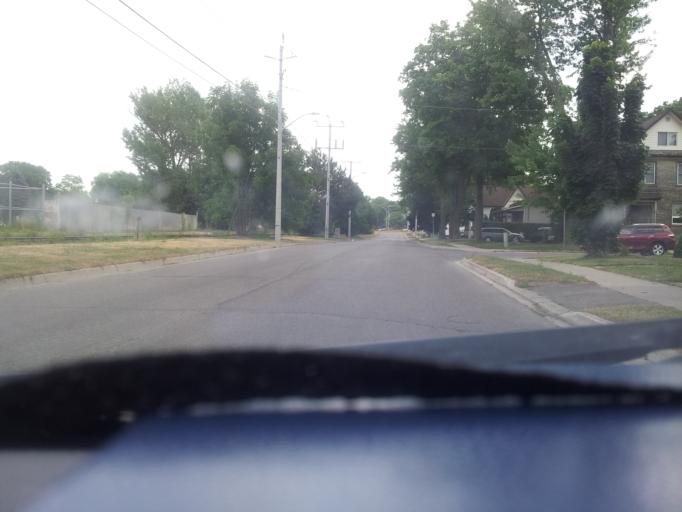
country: CA
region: Ontario
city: Stratford
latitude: 43.3655
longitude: -80.9819
